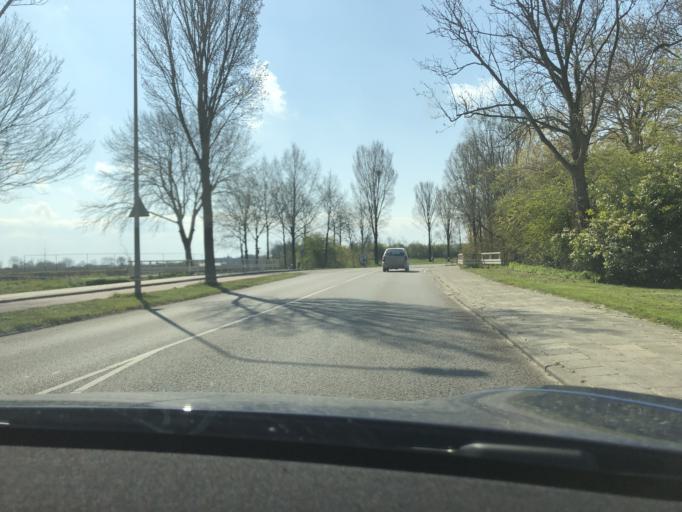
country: NL
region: Zeeland
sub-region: Gemeente Middelburg
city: Middelburg
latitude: 51.5015
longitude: 3.5942
